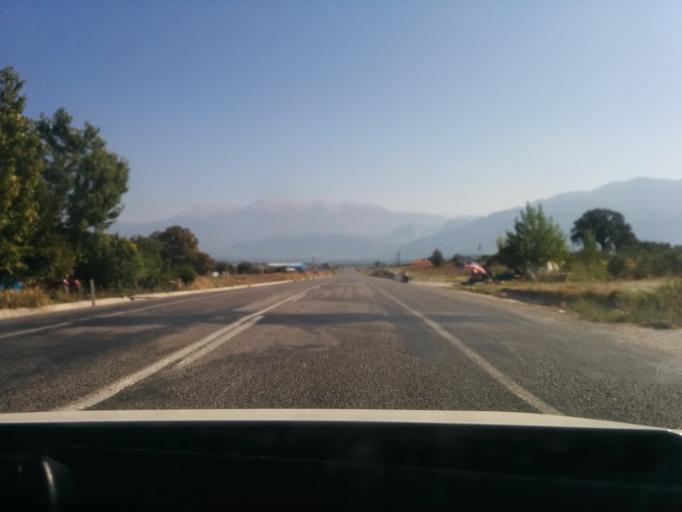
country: TR
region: Mugla
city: Esen
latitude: 36.4409
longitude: 29.2754
